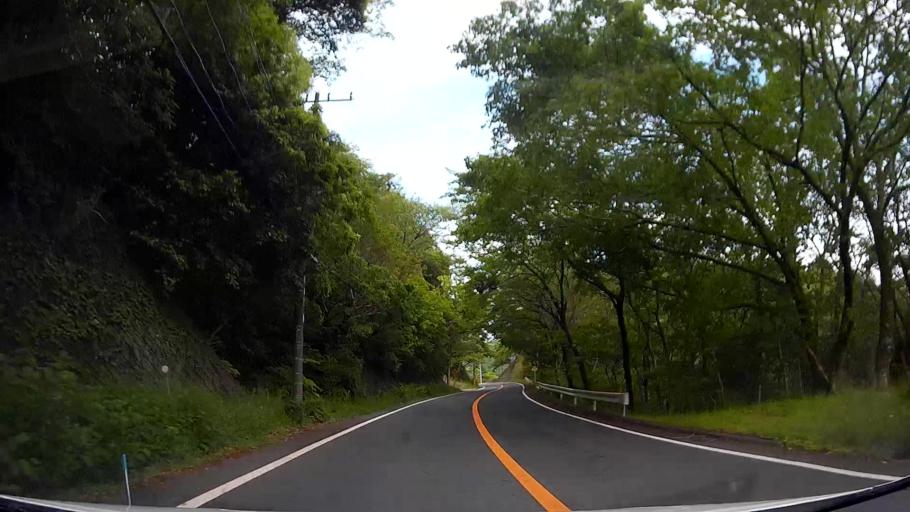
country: JP
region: Shizuoka
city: Heda
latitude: 34.9225
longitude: 138.8241
